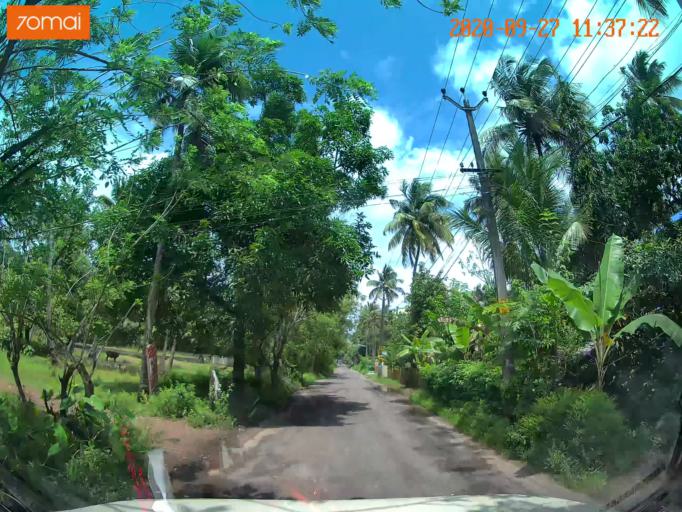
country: IN
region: Kerala
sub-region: Thrissur District
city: Thanniyam
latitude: 10.4549
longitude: 76.1232
